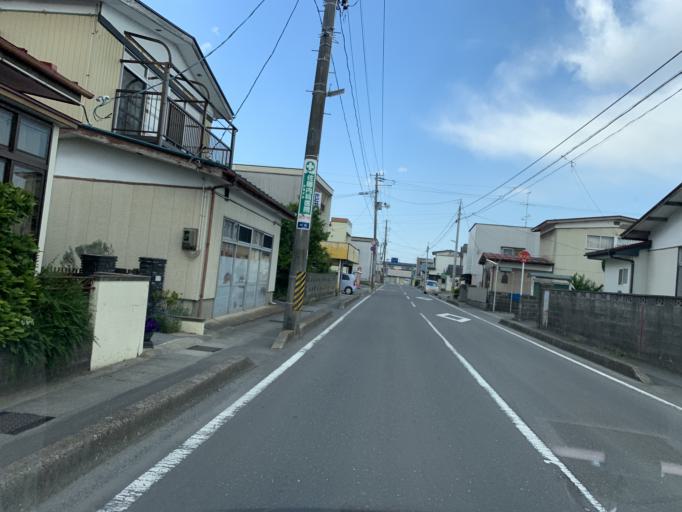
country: JP
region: Miyagi
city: Wakuya
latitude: 38.6293
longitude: 141.1974
